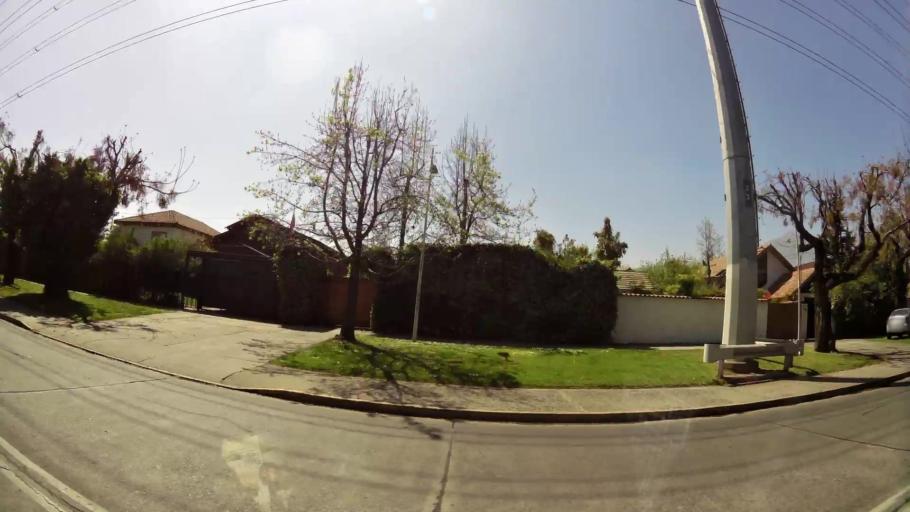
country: CL
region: Santiago Metropolitan
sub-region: Provincia de Santiago
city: Villa Presidente Frei, Nunoa, Santiago, Chile
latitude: -33.4225
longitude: -70.5483
